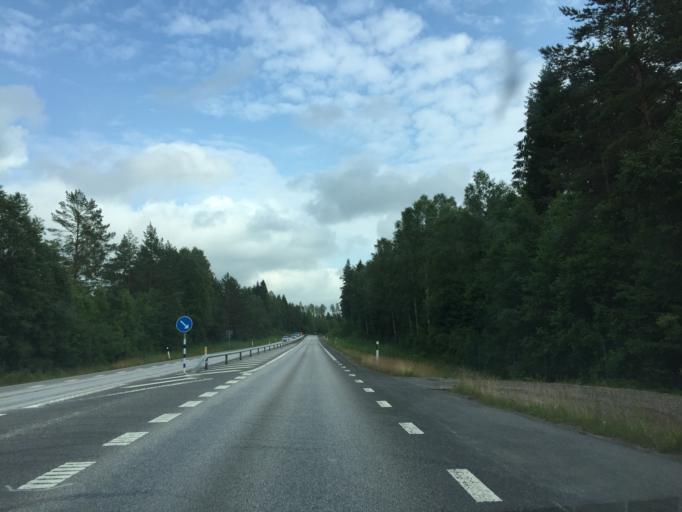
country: SE
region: OErebro
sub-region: Karlskoga Kommun
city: Karlskoga
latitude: 59.2956
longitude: 14.6647
